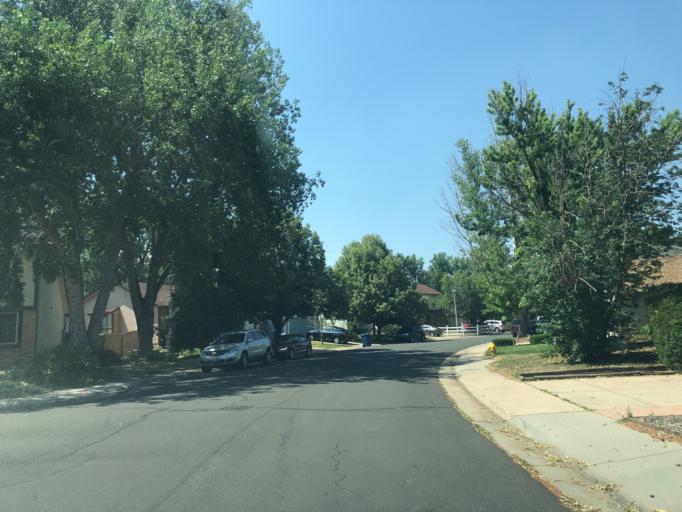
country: US
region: Colorado
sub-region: Arapahoe County
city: Dove Valley
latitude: 39.6326
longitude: -104.7850
